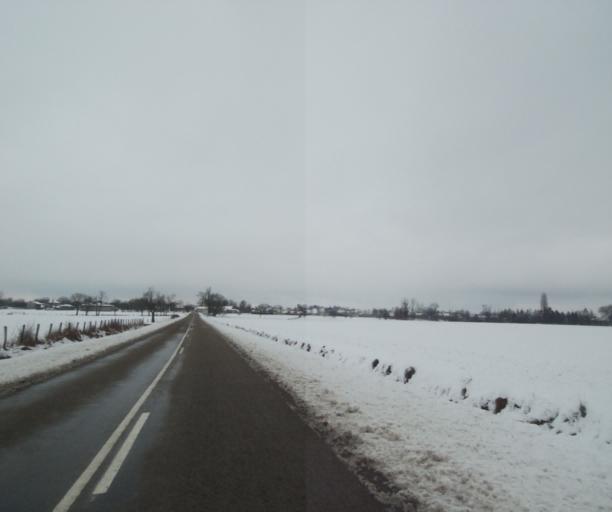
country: FR
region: Champagne-Ardenne
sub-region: Departement de la Haute-Marne
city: Montier-en-Der
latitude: 48.4780
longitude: 4.7874
